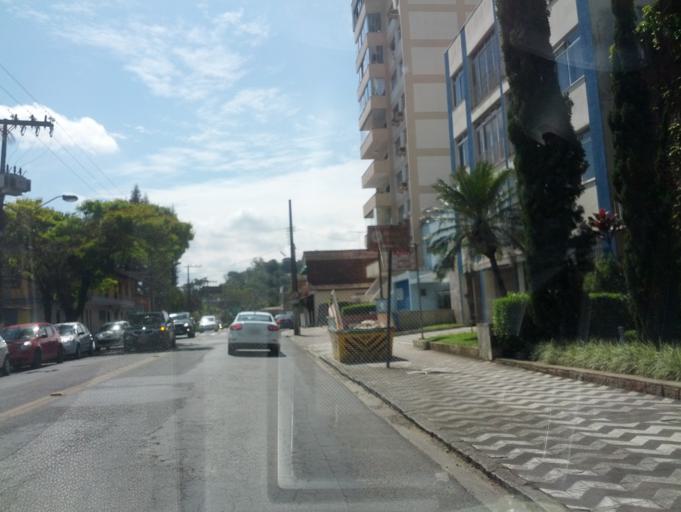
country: BR
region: Santa Catarina
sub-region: Blumenau
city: Blumenau
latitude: -26.9156
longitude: -49.0650
